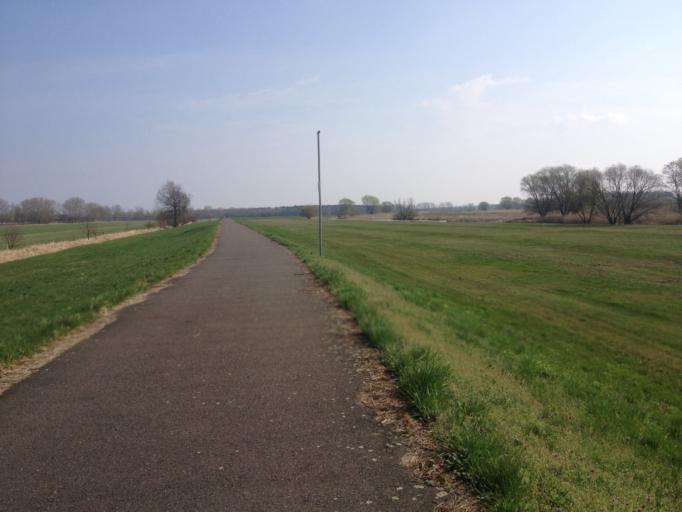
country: DE
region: Brandenburg
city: Briesen
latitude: 51.8451
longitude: 14.2585
